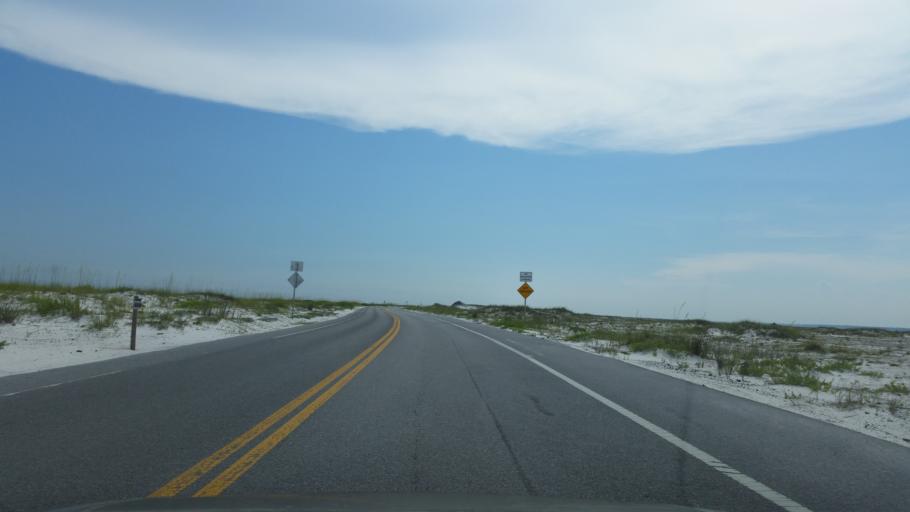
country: US
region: Florida
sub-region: Santa Rosa County
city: Woodlawn Beach
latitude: 30.3704
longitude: -86.9285
